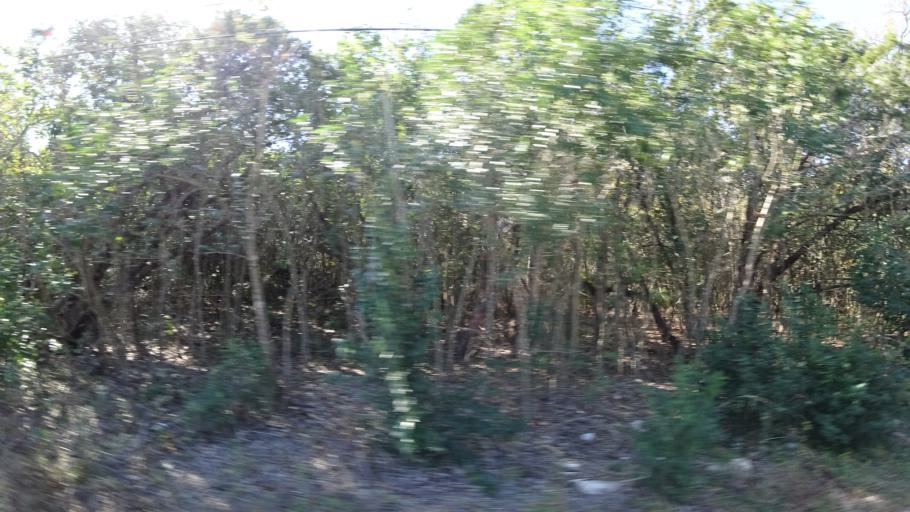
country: US
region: Texas
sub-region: Travis County
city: Barton Creek
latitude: 30.2264
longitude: -97.8555
